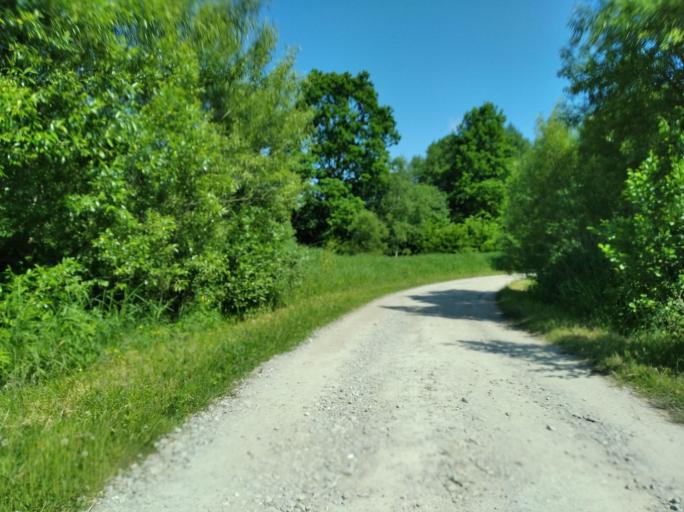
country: PL
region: Subcarpathian Voivodeship
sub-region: Powiat krosnienski
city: Odrzykon
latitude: 49.7777
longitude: 21.7608
